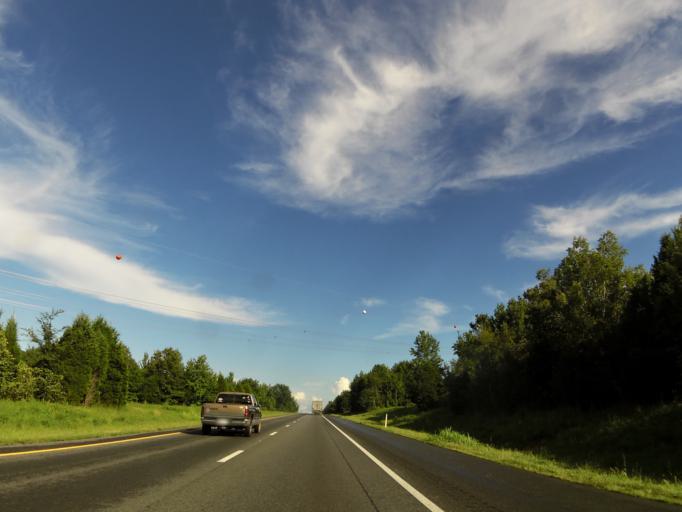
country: US
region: Kentucky
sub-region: Todd County
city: Guthrie
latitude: 36.5120
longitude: -87.2045
